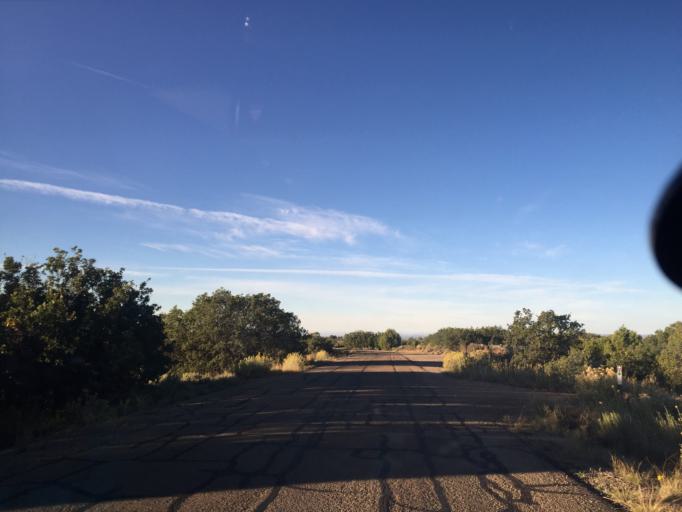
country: US
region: Utah
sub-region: San Juan County
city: Blanding
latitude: 37.7327
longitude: -109.4137
